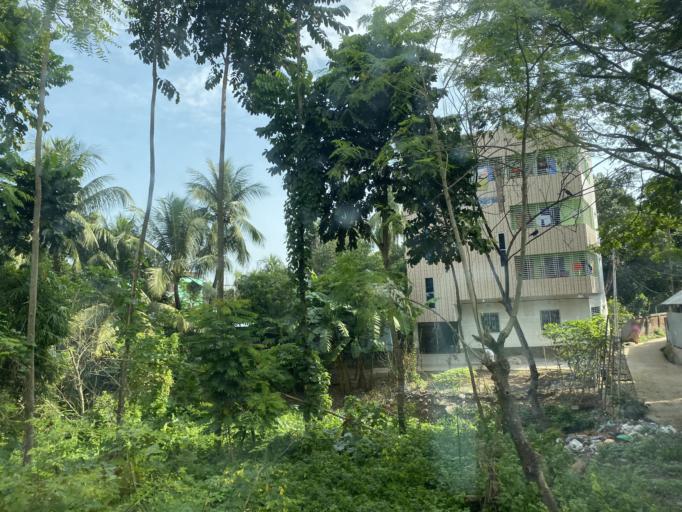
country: BD
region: Dhaka
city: Bhairab Bazar
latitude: 23.9651
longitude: 91.1169
